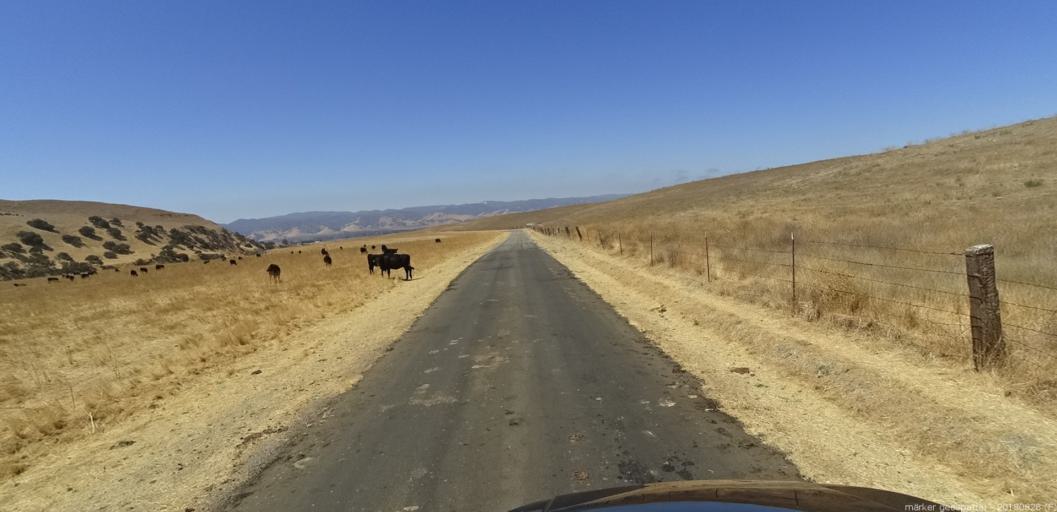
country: US
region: California
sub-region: San Luis Obispo County
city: Lake Nacimiento
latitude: 36.0305
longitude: -120.8618
